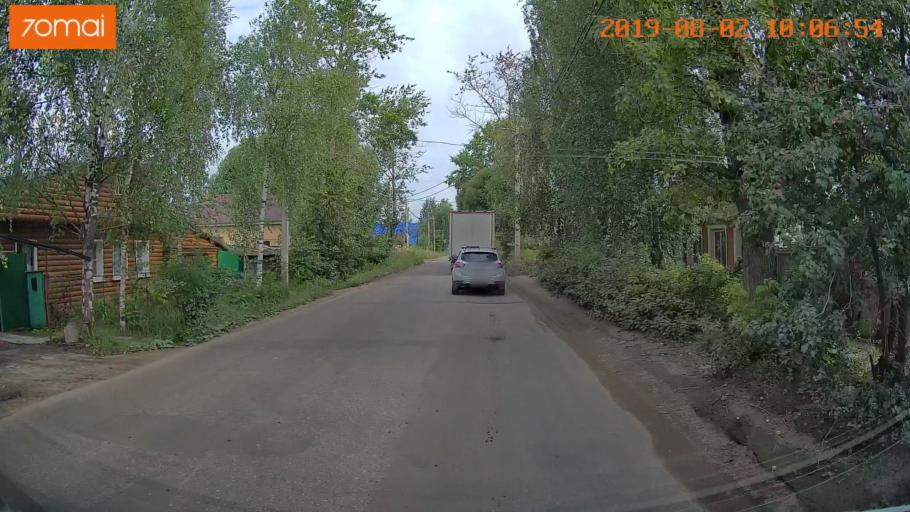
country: RU
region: Ivanovo
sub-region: Gorod Ivanovo
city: Ivanovo
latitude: 56.9811
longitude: 40.9355
